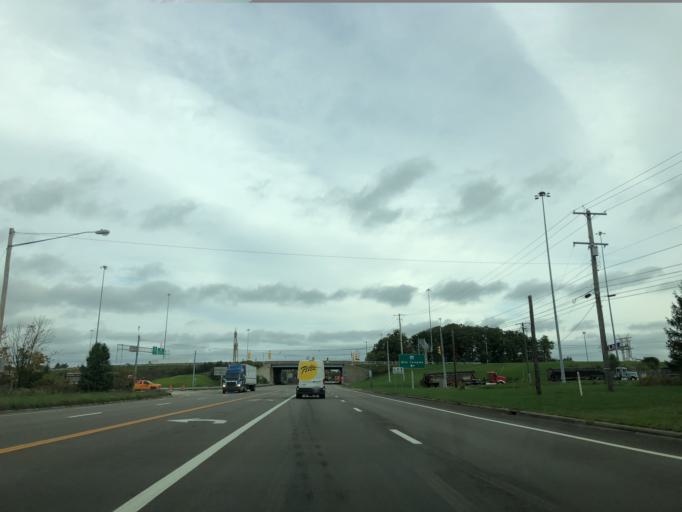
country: US
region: Ohio
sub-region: Summit County
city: Richfield
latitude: 41.2690
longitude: -81.6286
